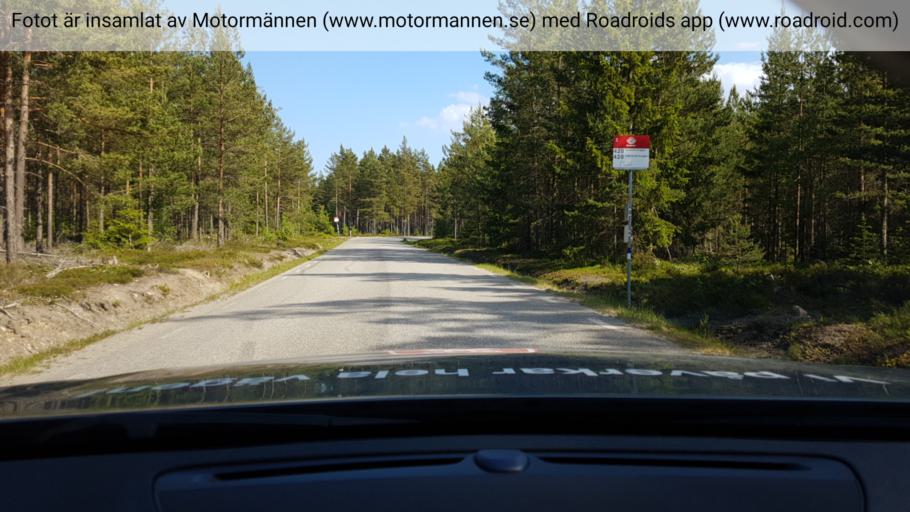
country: SE
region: Stockholm
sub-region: Varmdo Kommun
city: Mortnas
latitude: 59.2544
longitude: 18.4479
